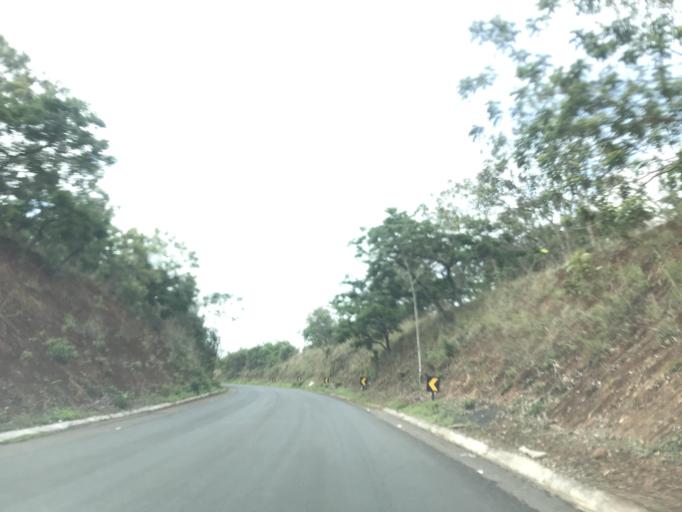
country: BR
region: Goias
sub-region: Bela Vista De Goias
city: Bela Vista de Goias
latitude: -17.0084
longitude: -48.6623
